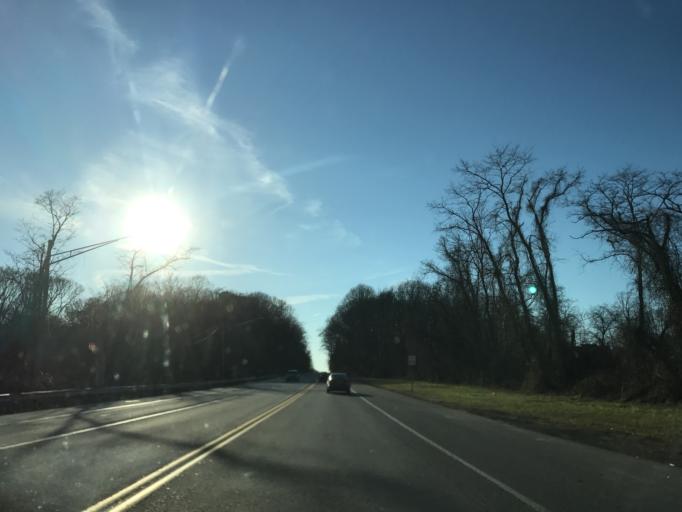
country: US
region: Maryland
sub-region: Anne Arundel County
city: Cape Saint Claire
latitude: 39.0361
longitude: -76.4570
